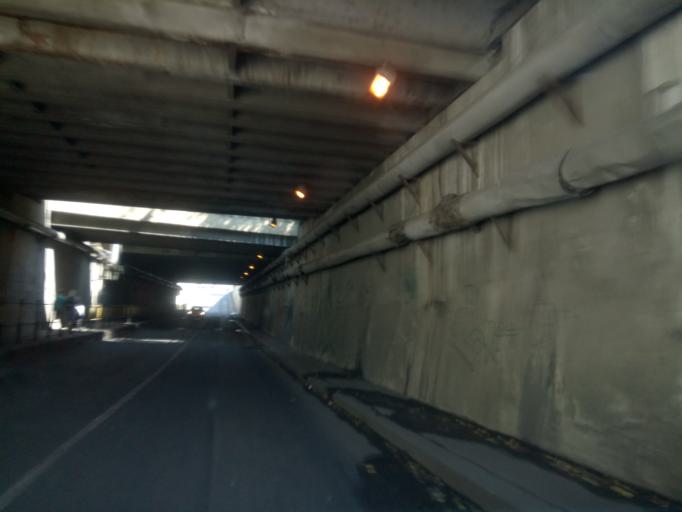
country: RS
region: Central Serbia
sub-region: Belgrade
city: Stari Grad
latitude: 44.8285
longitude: 20.4562
